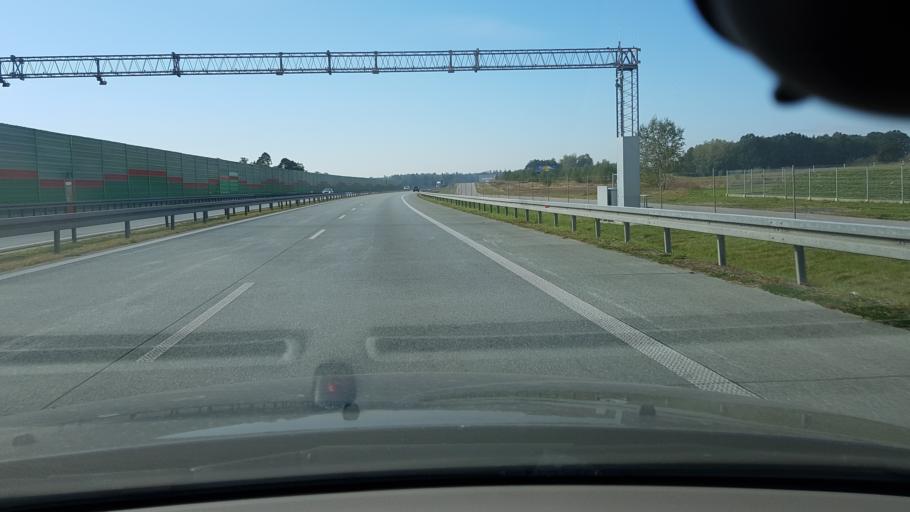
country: PL
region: Lodz Voivodeship
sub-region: Powiat tomaszowski
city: Lubochnia
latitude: 51.5998
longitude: 20.0575
